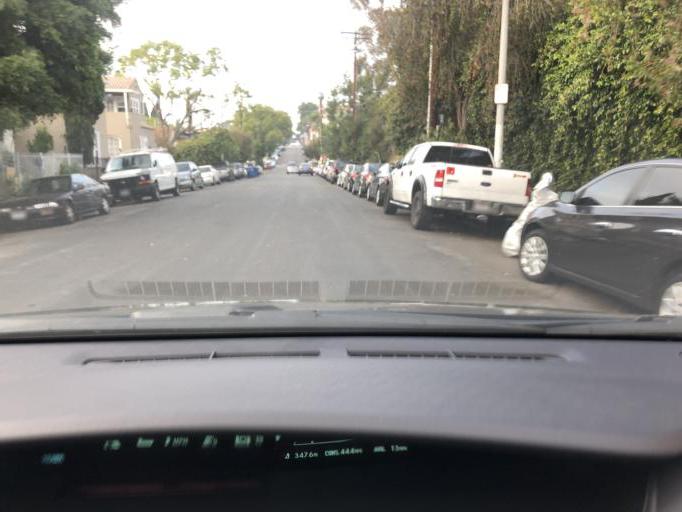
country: US
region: California
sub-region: Los Angeles County
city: Echo Park
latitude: 34.0635
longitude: -118.2794
